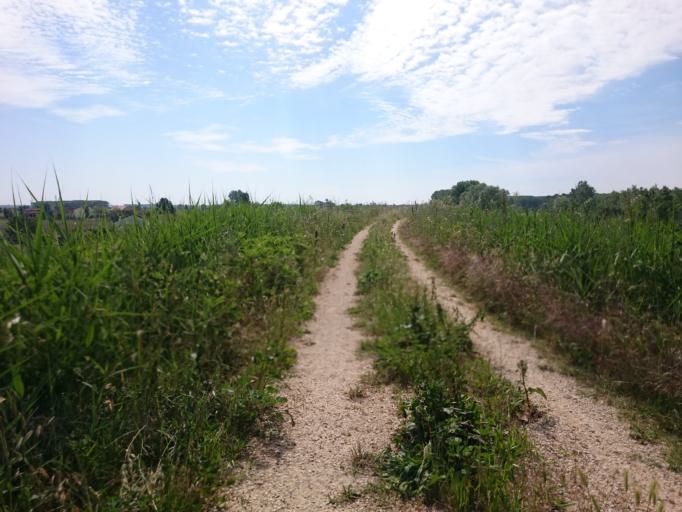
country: IT
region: Veneto
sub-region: Provincia di Rovigo
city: Ariano
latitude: 44.9609
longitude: 12.1140
